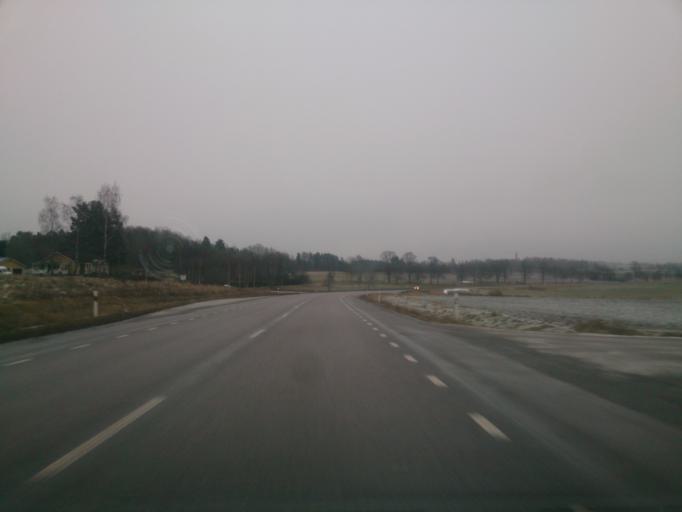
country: SE
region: OEstergoetland
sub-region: Atvidabergs Kommun
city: Atvidaberg
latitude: 58.2354
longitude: 15.9536
